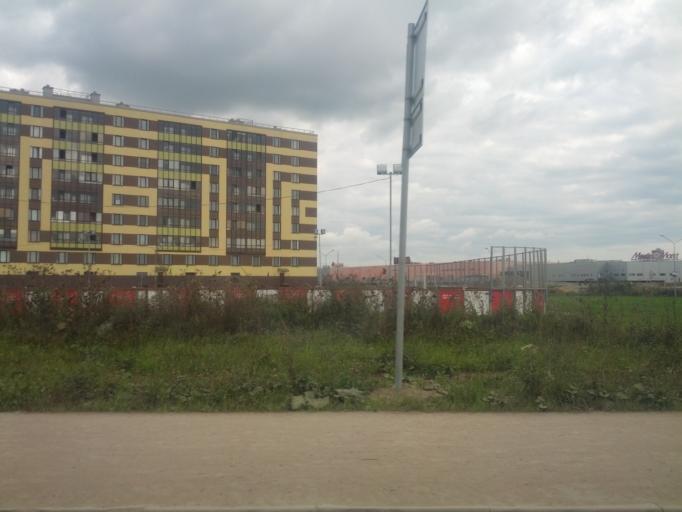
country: RU
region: Leningrad
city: Rybatskoye
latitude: 59.8959
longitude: 30.5043
